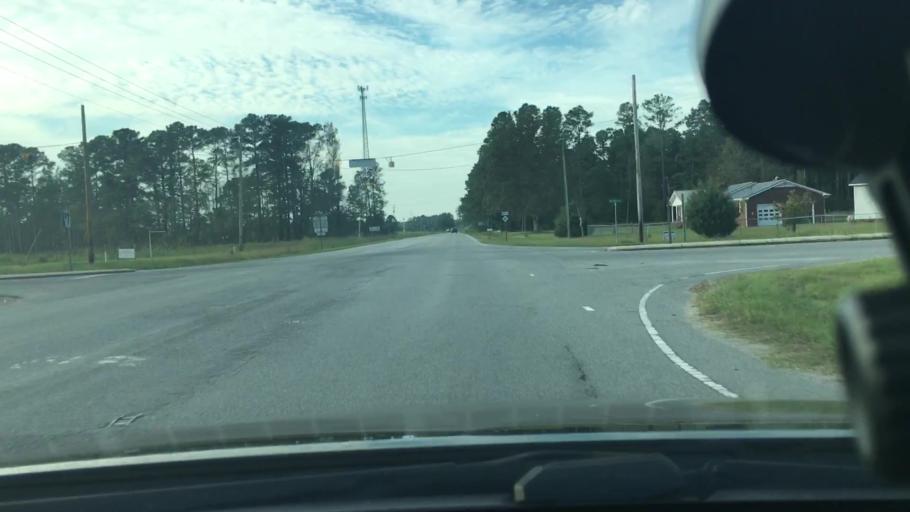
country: US
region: North Carolina
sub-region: Craven County
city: Vanceboro
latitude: 35.4182
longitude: -77.2562
